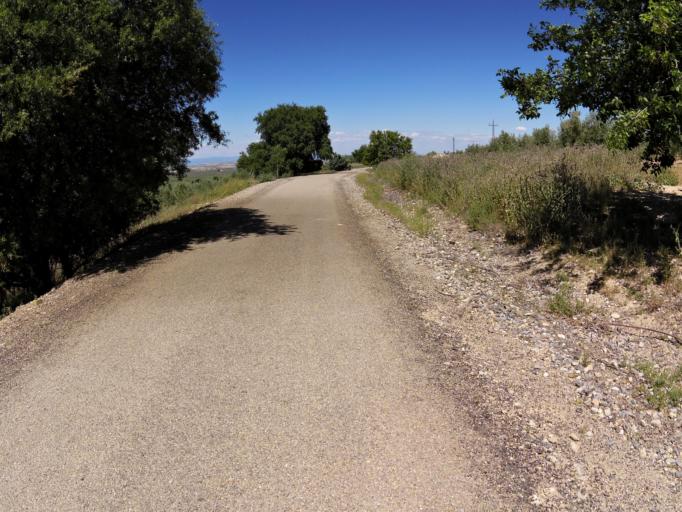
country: ES
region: Andalusia
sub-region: Provincia de Jaen
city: Torre del Campo
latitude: 37.7881
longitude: -3.8886
